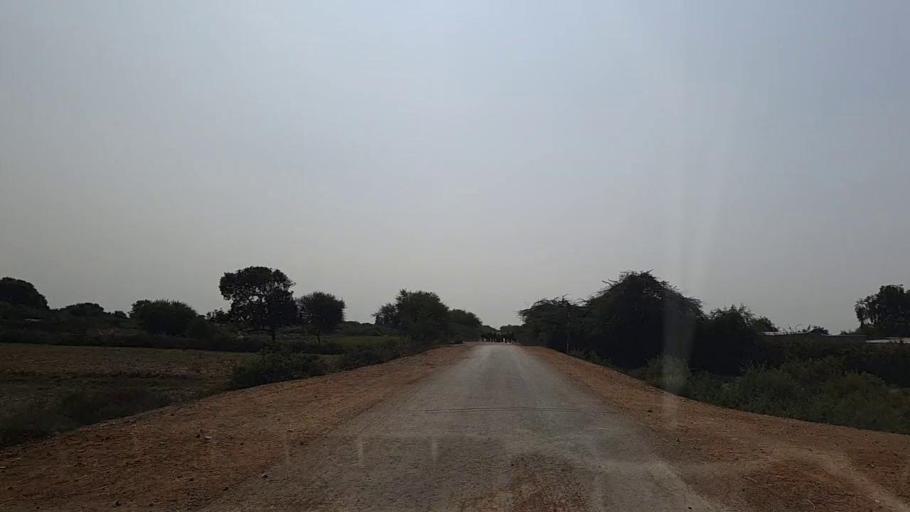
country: PK
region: Sindh
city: Chuhar Jamali
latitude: 24.2549
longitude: 67.9067
